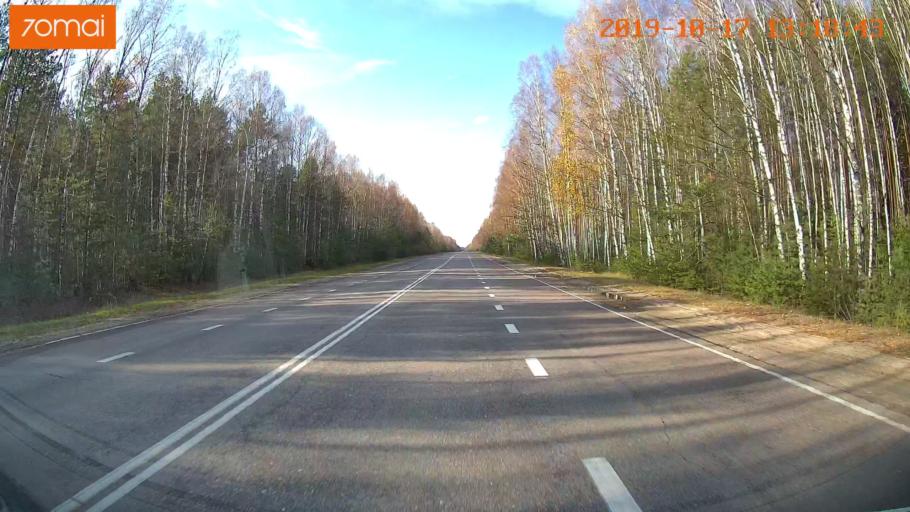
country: RU
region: Rjazan
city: Gus'-Zheleznyy
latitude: 55.0647
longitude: 41.0913
